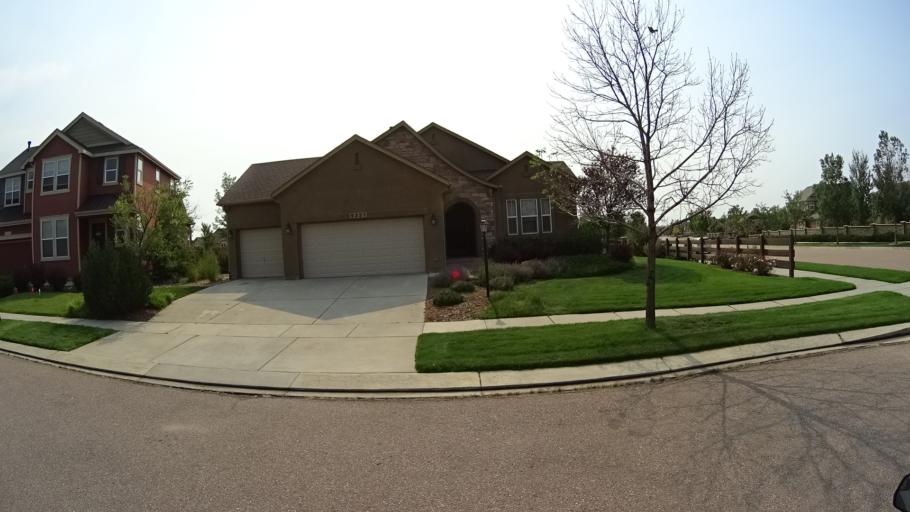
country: US
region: Colorado
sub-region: El Paso County
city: Black Forest
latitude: 38.9670
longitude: -104.7338
